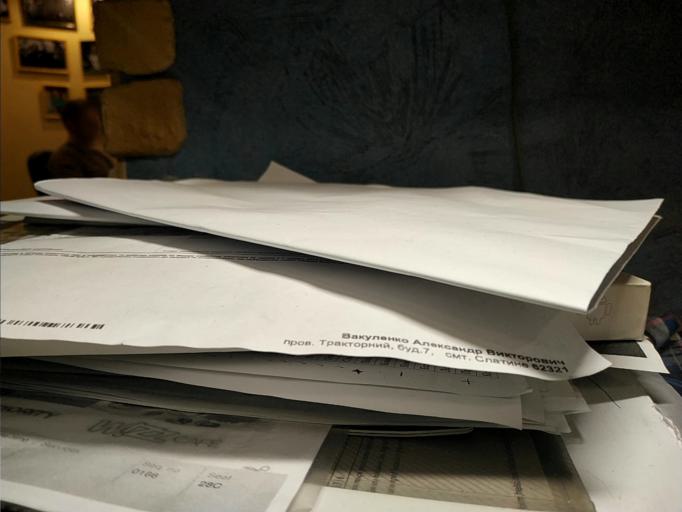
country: RU
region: Tverskaya
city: Zubtsov
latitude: 56.1080
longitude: 34.6432
